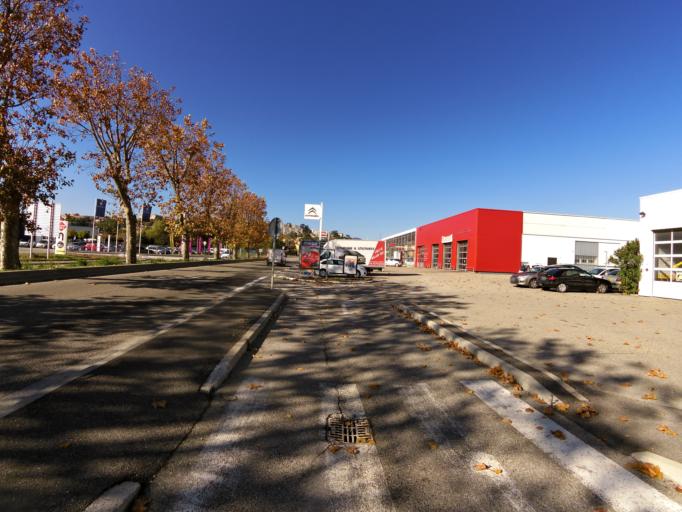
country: FR
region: Rhone-Alpes
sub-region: Departement de l'Ardeche
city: Aubenas
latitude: 44.6136
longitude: 4.4071
